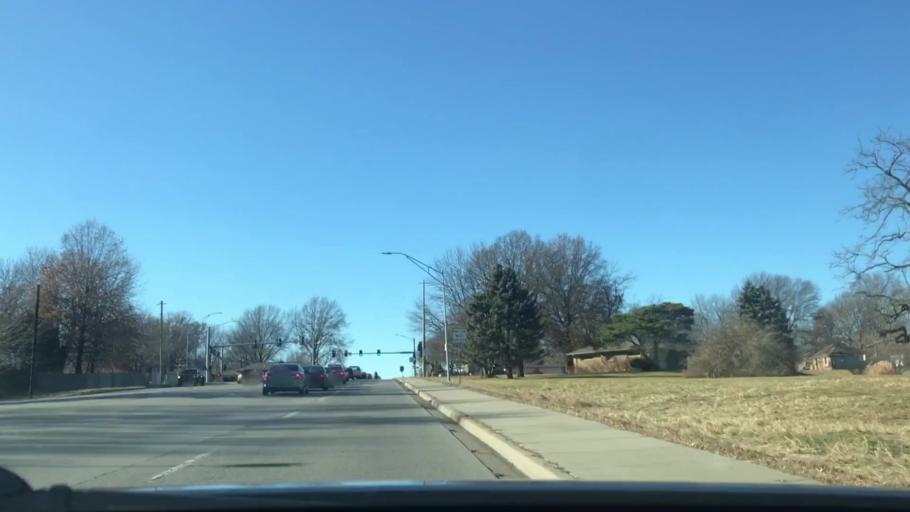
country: US
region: Missouri
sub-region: Jackson County
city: Independence
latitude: 39.0490
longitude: -94.3855
